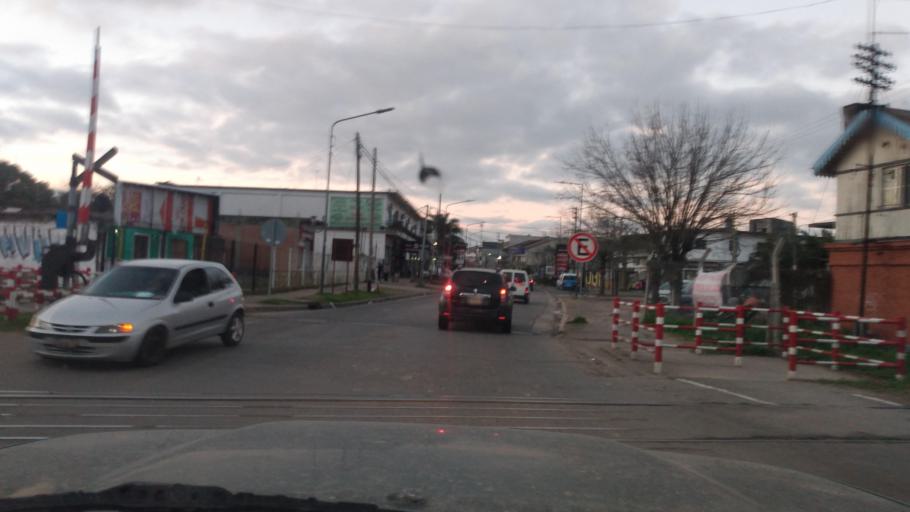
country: AR
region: Buenos Aires
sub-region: Partido de Pilar
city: Pilar
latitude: -34.4664
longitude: -58.9153
